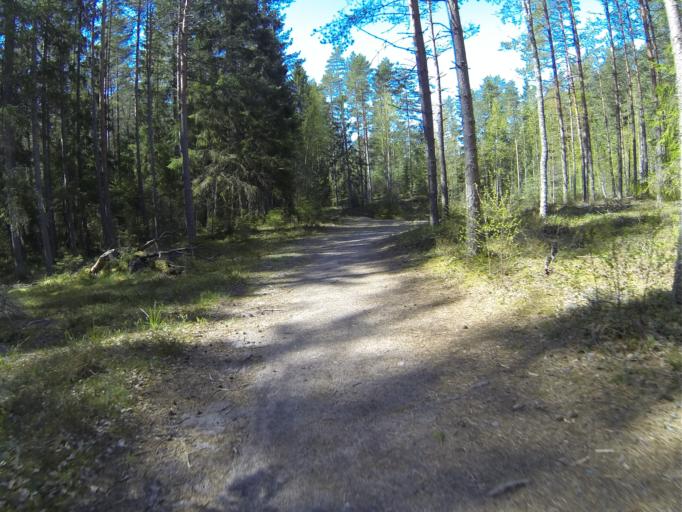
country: FI
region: Varsinais-Suomi
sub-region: Salo
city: Pertteli
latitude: 60.3962
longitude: 23.2072
